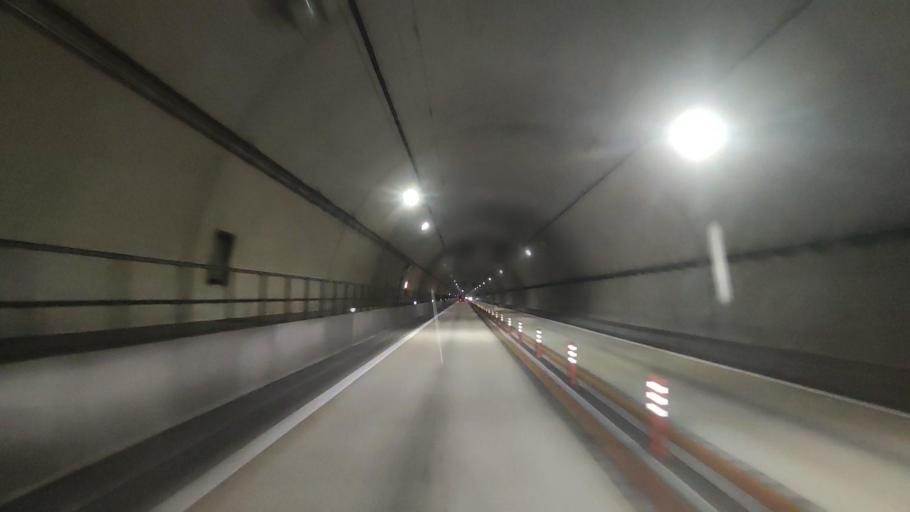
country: JP
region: Wakayama
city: Tanabe
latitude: 33.5673
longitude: 135.4910
